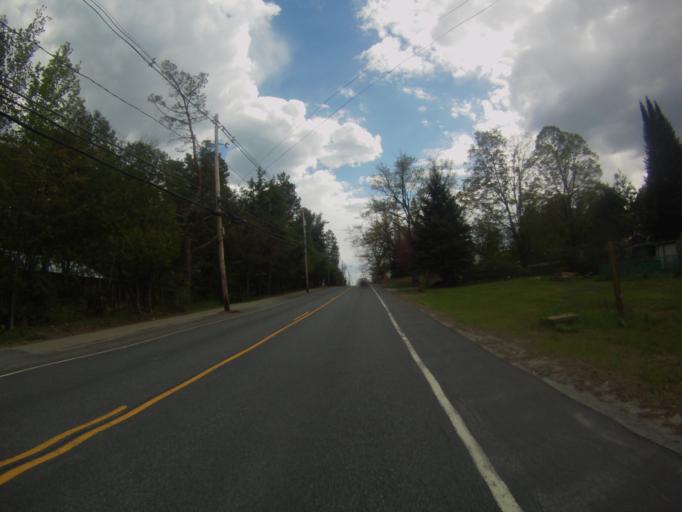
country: US
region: New York
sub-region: Essex County
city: Ticonderoga
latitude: 43.8454
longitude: -73.7590
